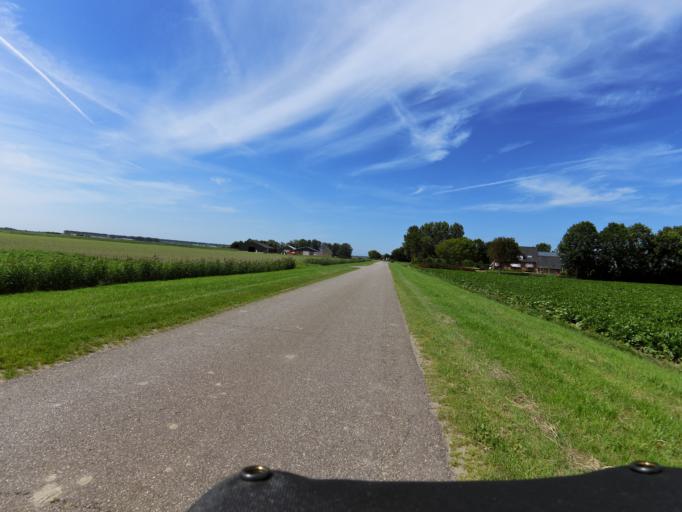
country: NL
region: South Holland
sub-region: Gemeente Goeree-Overflakkee
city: Dirksland
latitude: 51.7977
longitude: 4.0946
